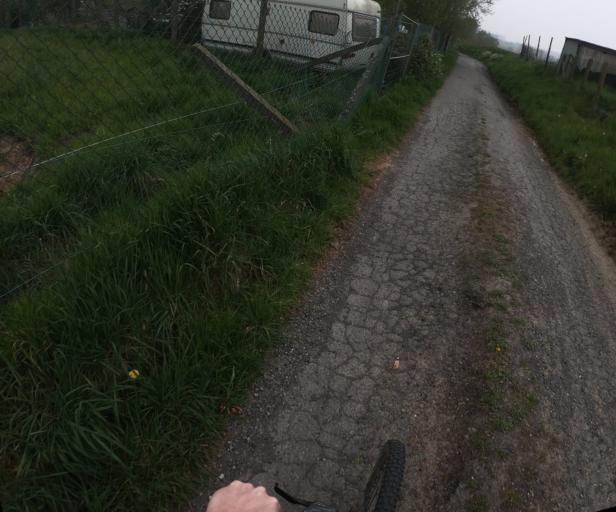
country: BE
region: Flanders
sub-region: Provincie Vlaams-Brabant
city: Pepingen
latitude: 50.7362
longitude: 4.1574
